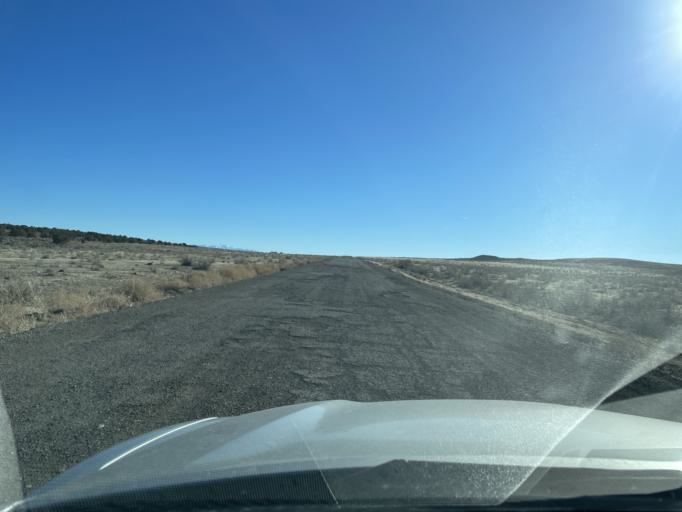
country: US
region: Colorado
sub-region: Mesa County
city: Loma
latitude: 39.1864
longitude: -109.1274
